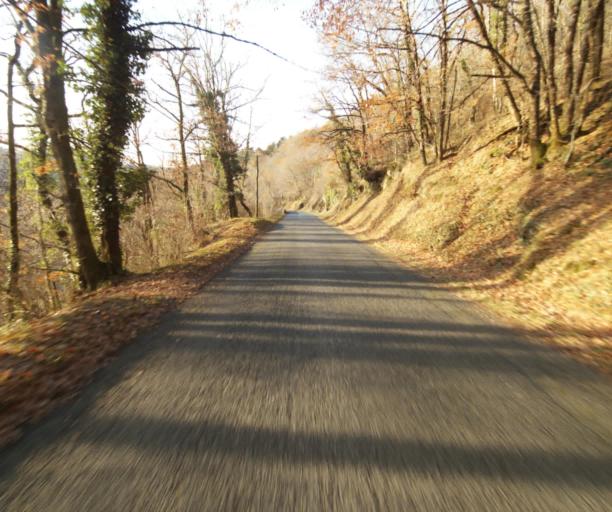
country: FR
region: Limousin
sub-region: Departement de la Correze
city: Laguenne
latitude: 45.2397
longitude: 1.7984
